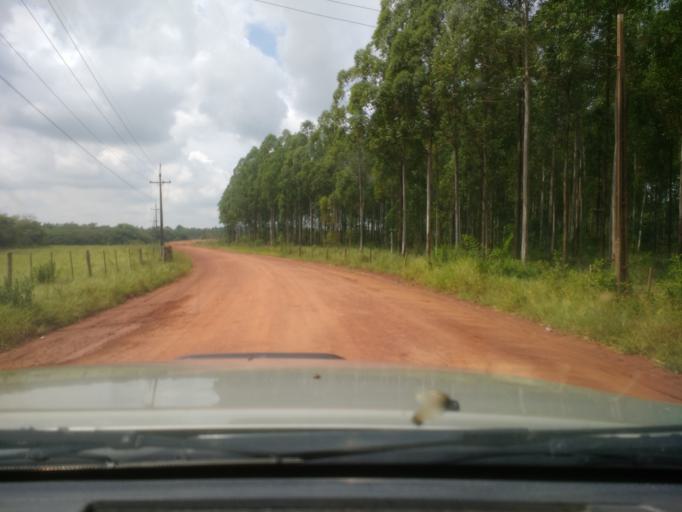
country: PY
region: San Pedro
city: Puerto Rosario
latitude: -24.4036
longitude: -57.1041
